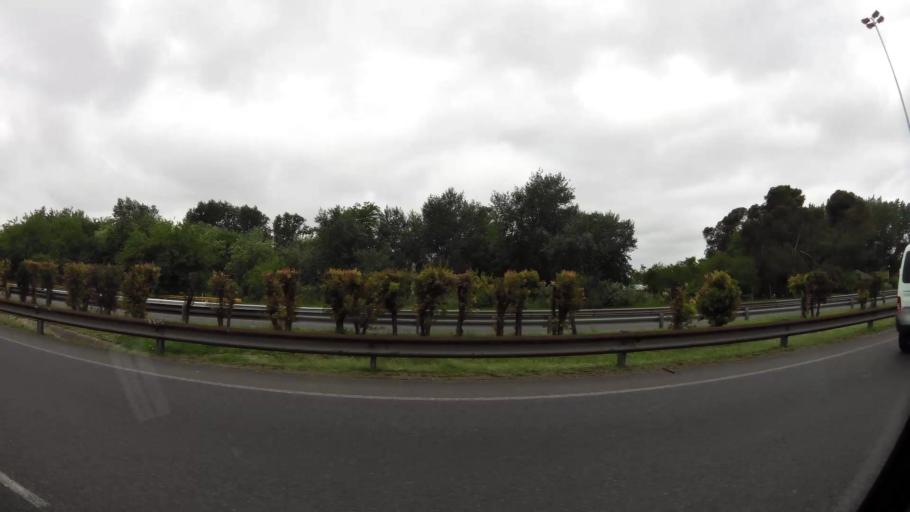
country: AR
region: Buenos Aires
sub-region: Partido de Ezeiza
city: Ezeiza
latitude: -34.8042
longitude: -58.5129
